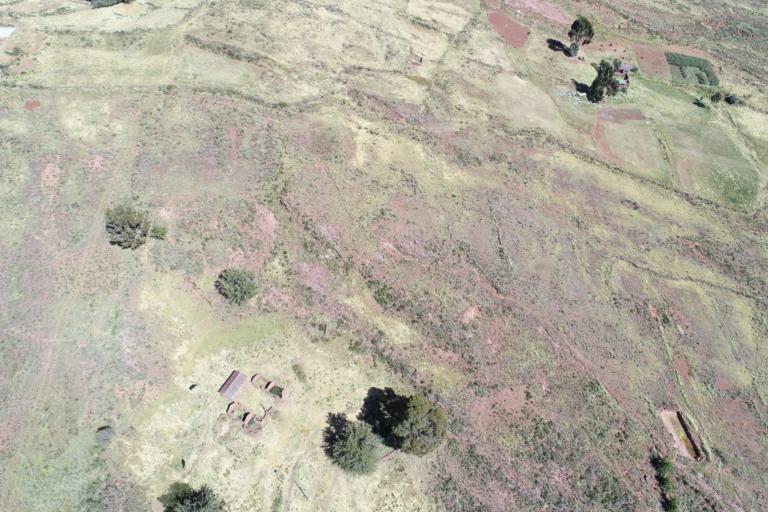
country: BO
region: La Paz
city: Tiahuanaco
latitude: -16.6084
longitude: -68.7639
